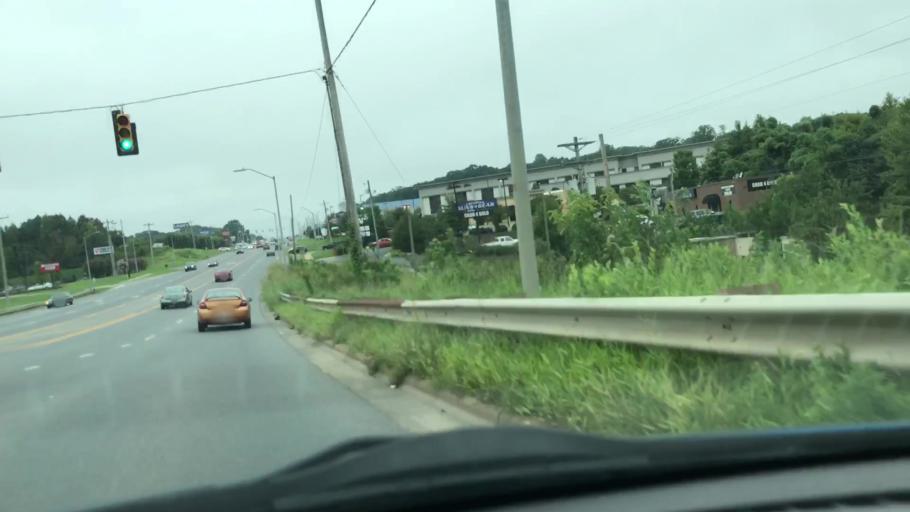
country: US
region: North Carolina
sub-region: Randolph County
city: Asheboro
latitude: 35.6964
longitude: -79.7904
